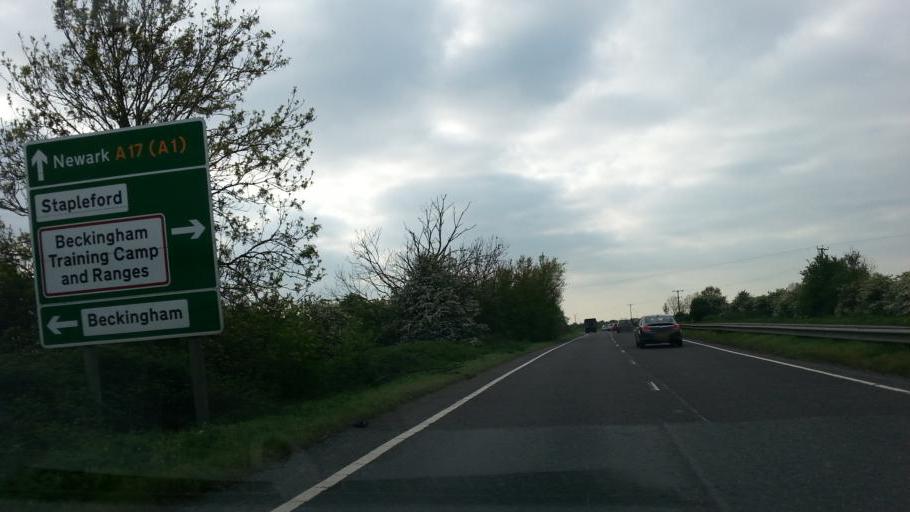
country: GB
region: England
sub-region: Nottinghamshire
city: South Collingham
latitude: 53.0734
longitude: -0.6876
